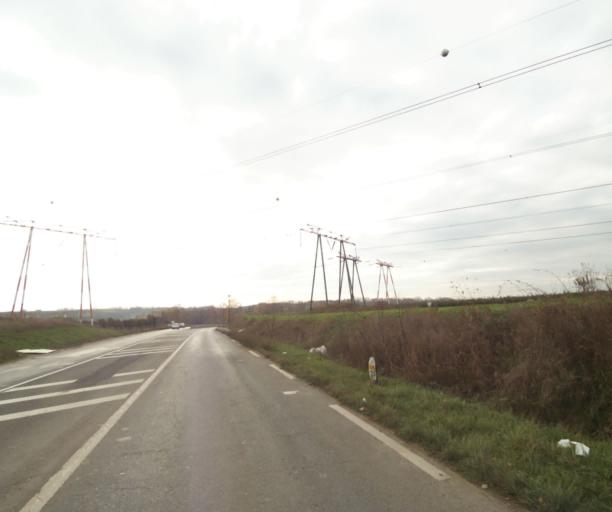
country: FR
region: Ile-de-France
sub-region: Departement du Val-d'Oise
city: Le Thillay
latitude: 49.0009
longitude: 2.4646
